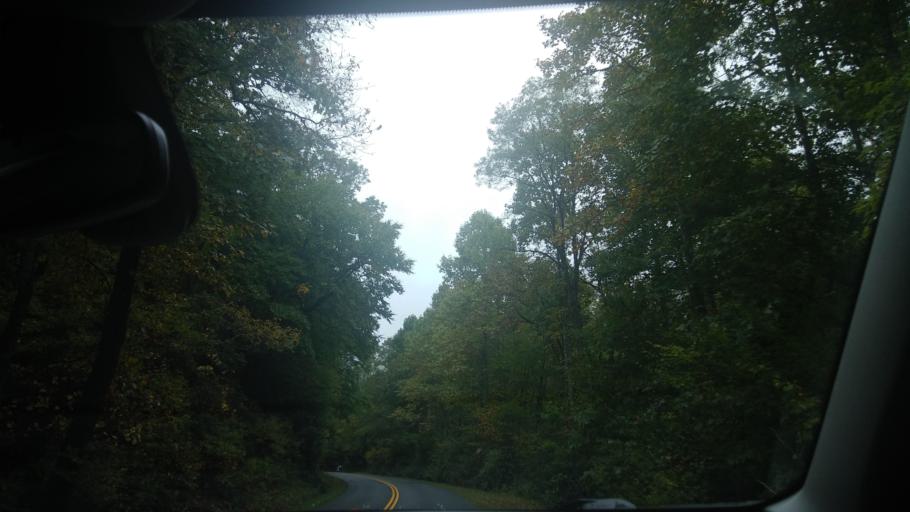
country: US
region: North Carolina
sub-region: Mitchell County
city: Spruce Pine
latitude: 35.9085
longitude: -81.9679
